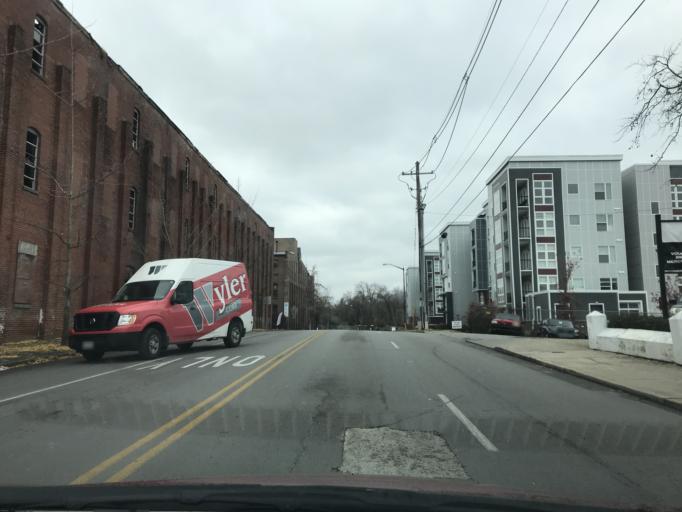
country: US
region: Indiana
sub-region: Clark County
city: Jeffersonville
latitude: 38.2507
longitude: -85.7212
